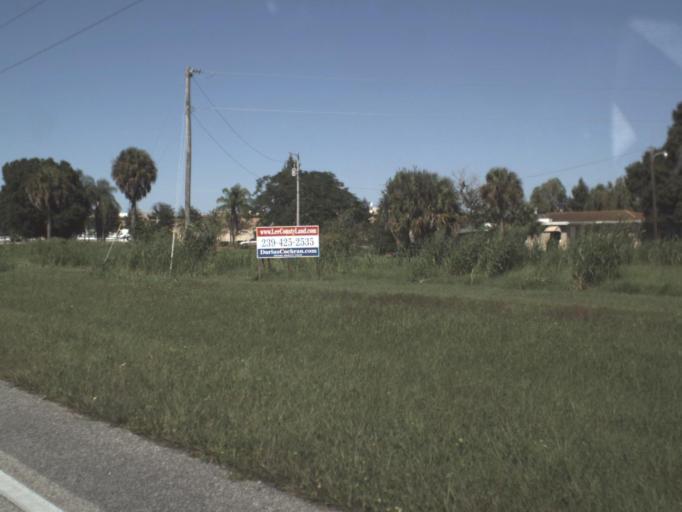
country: US
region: Florida
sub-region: Lee County
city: Palmona Park
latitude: 26.6770
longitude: -81.8986
